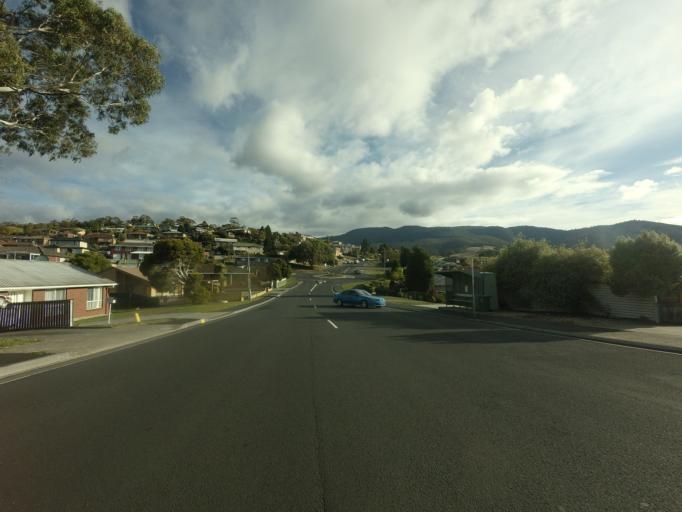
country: AU
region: Tasmania
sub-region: Glenorchy
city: Austins Ferry
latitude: -42.7731
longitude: 147.2448
